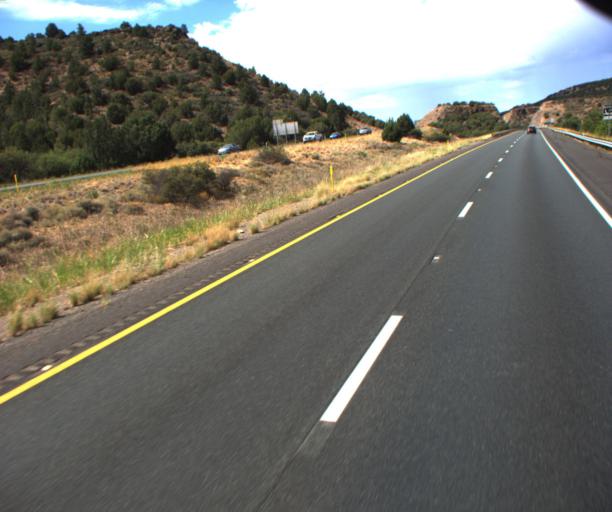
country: US
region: Arizona
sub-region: Yavapai County
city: Camp Verde
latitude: 34.5064
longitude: -111.9984
